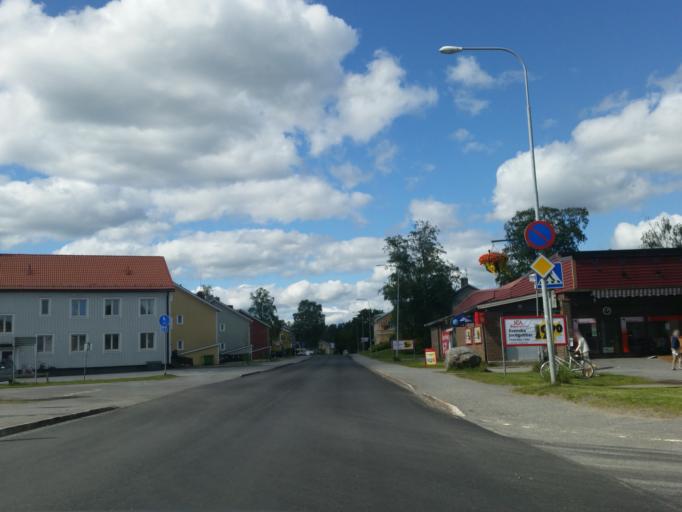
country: SE
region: Vaesterbotten
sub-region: Robertsfors Kommun
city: Robertsfors
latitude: 64.1936
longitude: 20.8474
